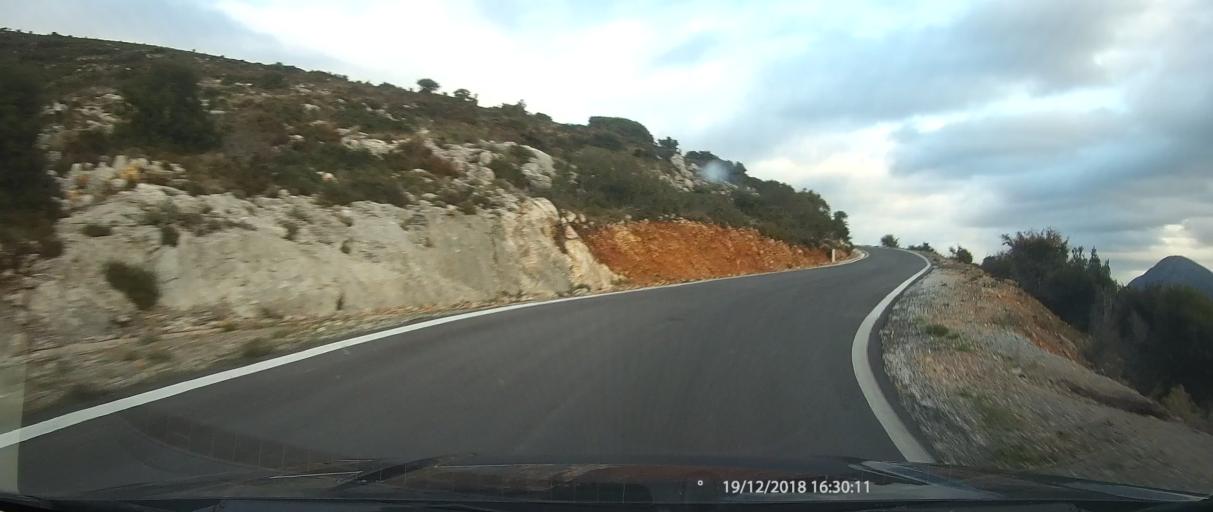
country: GR
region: Peloponnese
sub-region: Nomos Lakonias
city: Molaoi
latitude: 36.9614
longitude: 22.8808
